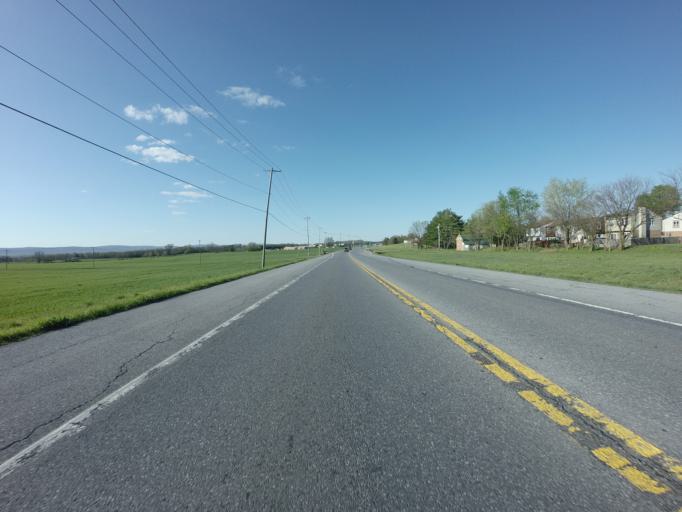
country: US
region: Maryland
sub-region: Frederick County
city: Walkersville
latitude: 39.4668
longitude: -77.3637
